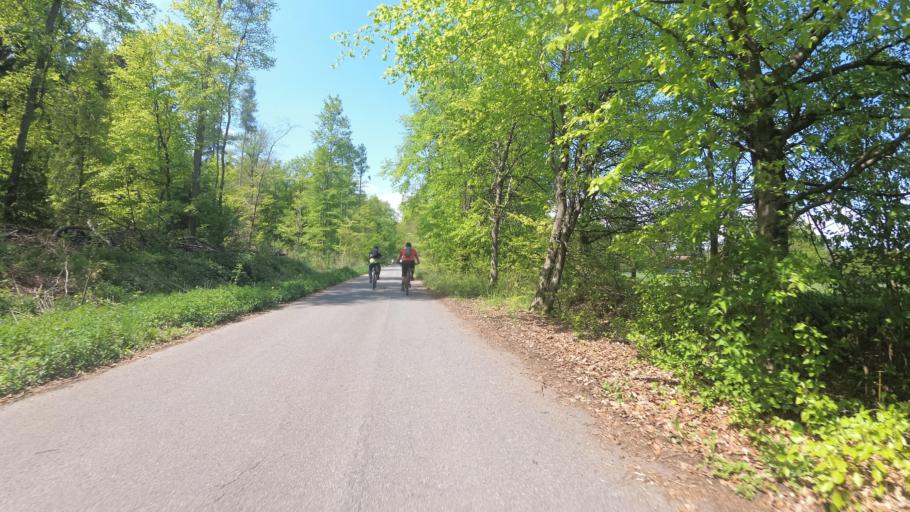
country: DE
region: Rheinland-Pfalz
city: Schonenberg-Kubelberg
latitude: 49.3776
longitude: 7.3785
